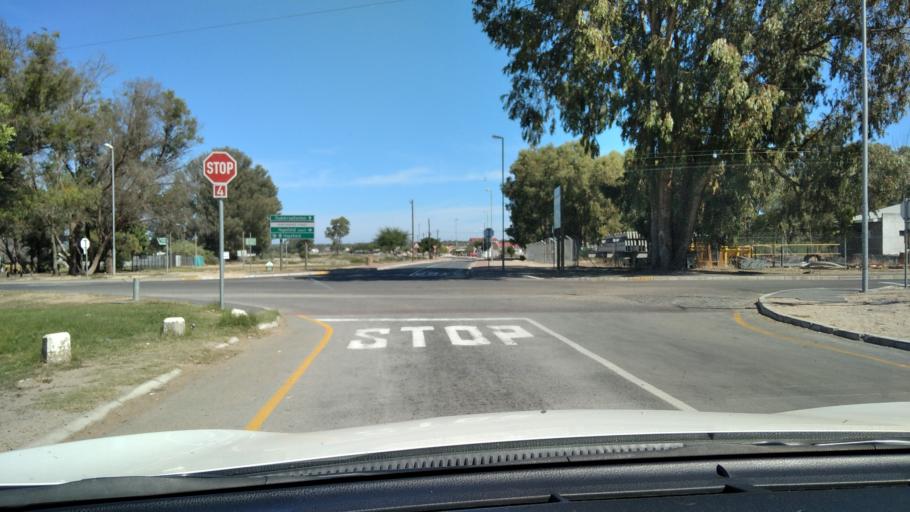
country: ZA
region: Western Cape
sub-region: West Coast District Municipality
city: Moorreesburg
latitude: -33.0596
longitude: 18.3418
